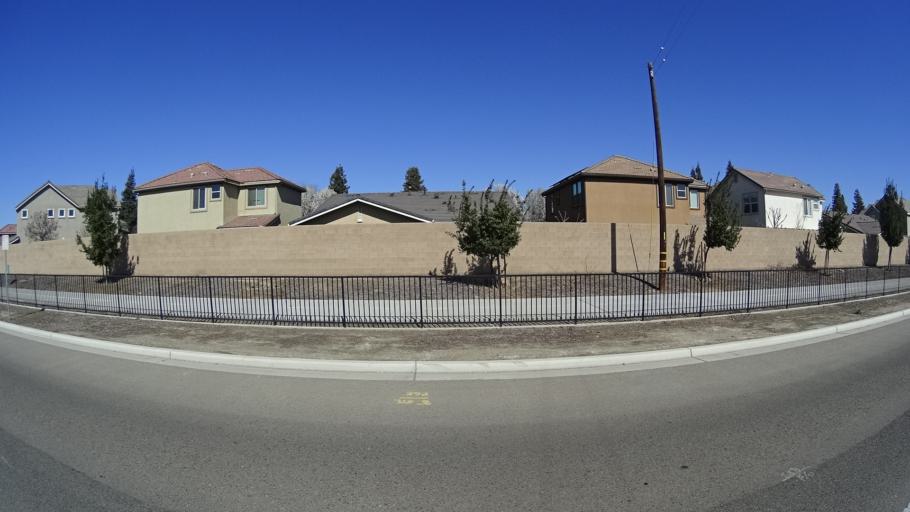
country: US
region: California
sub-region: Fresno County
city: Biola
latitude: 36.8370
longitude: -119.8961
